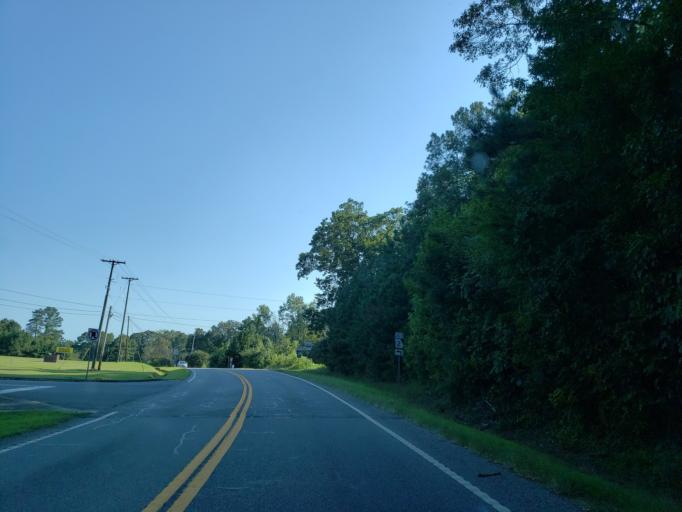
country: US
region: Georgia
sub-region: Whitfield County
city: Varnell
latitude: 34.8994
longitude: -84.9766
